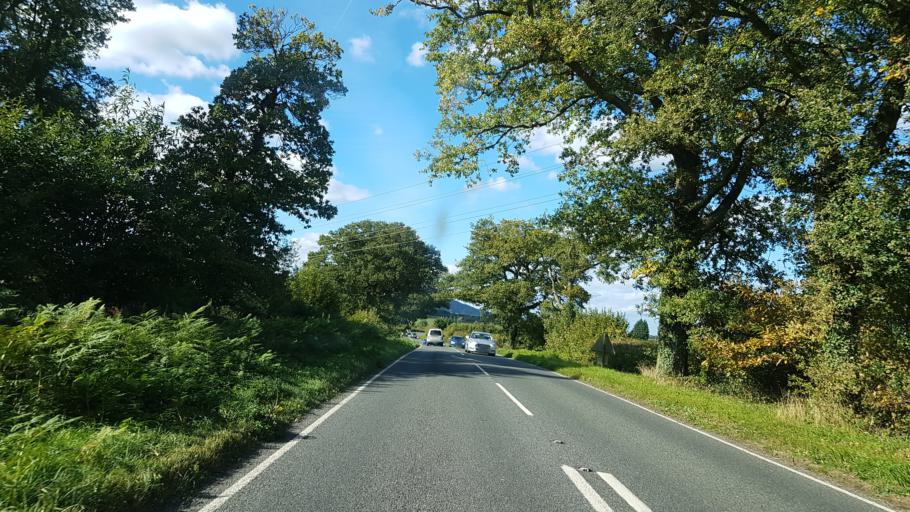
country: GB
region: England
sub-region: West Sussex
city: Petworth
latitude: 51.0370
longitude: -0.6376
